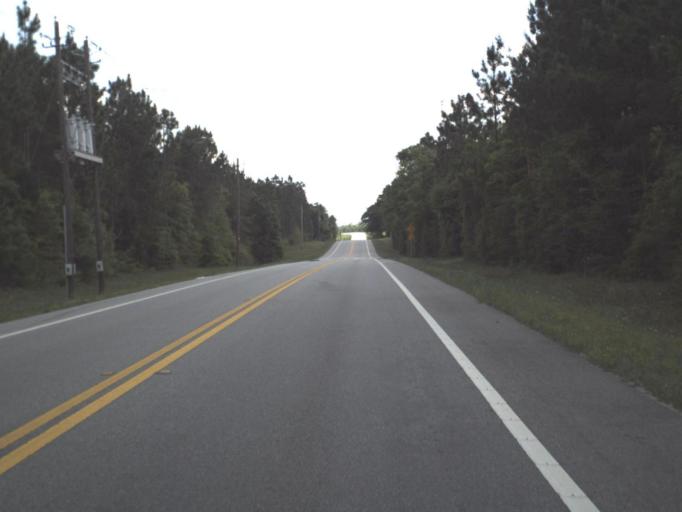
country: US
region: Florida
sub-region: Escambia County
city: Molino
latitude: 30.7565
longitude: -87.3790
